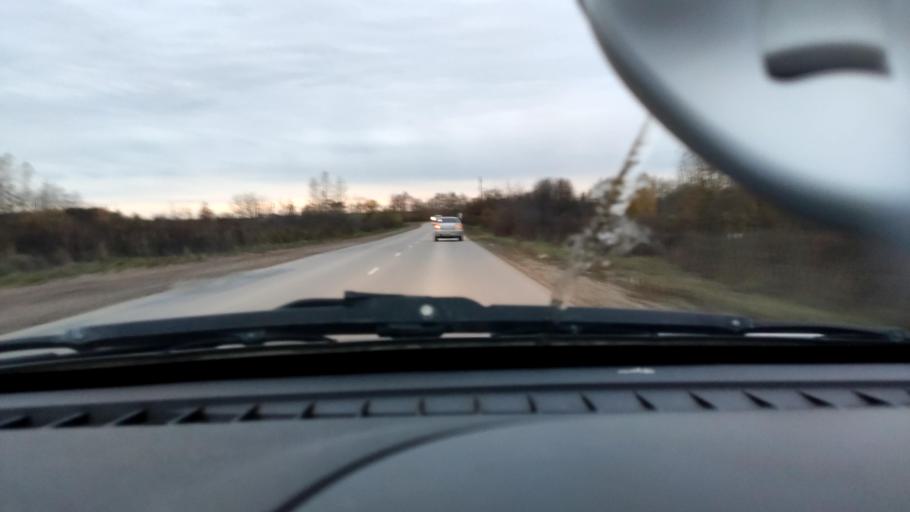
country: RU
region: Perm
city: Kondratovo
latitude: 58.0038
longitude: 56.0608
